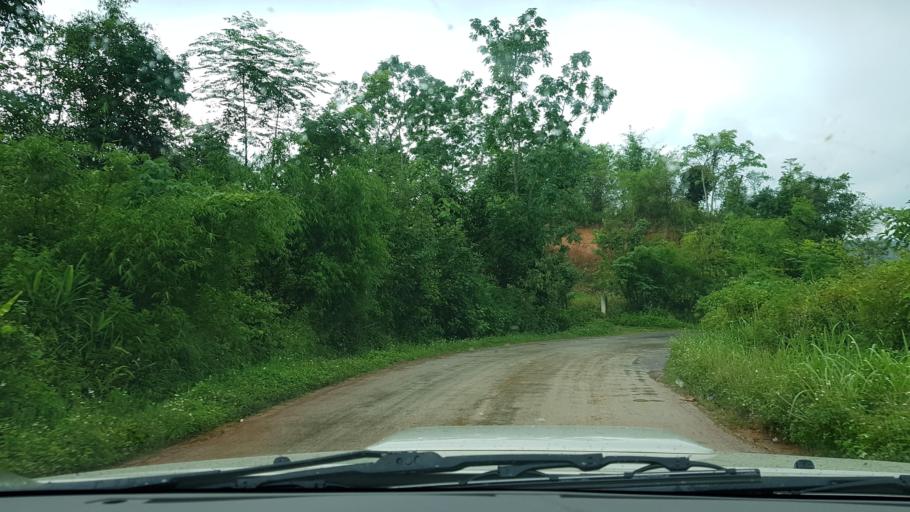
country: LA
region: Oudomxai
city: Muang Xay
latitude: 20.5762
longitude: 101.9225
